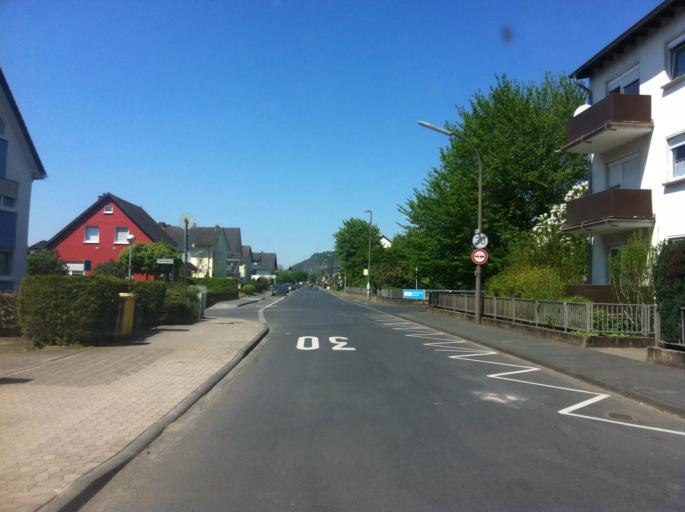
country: DE
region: Rheinland-Pfalz
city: Ockenfels
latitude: 50.5631
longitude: 7.2663
